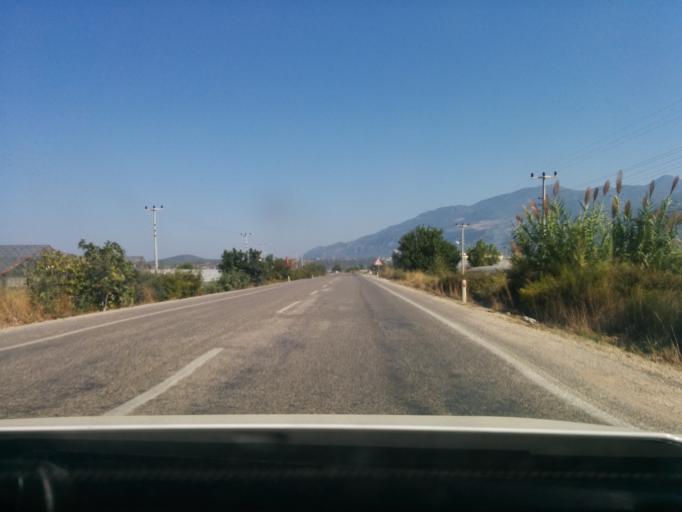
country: TR
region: Antalya
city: Kalkan
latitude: 36.3280
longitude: 29.3324
